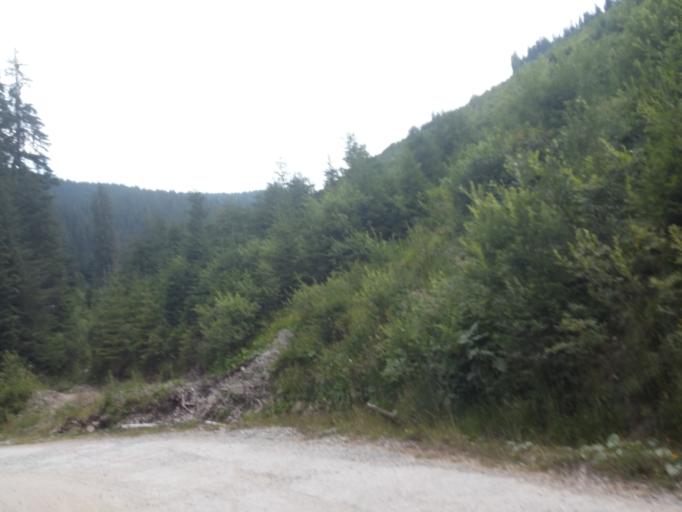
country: RO
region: Valcea
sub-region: Comuna Voineasa
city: Voineasa
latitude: 45.4369
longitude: 23.7646
